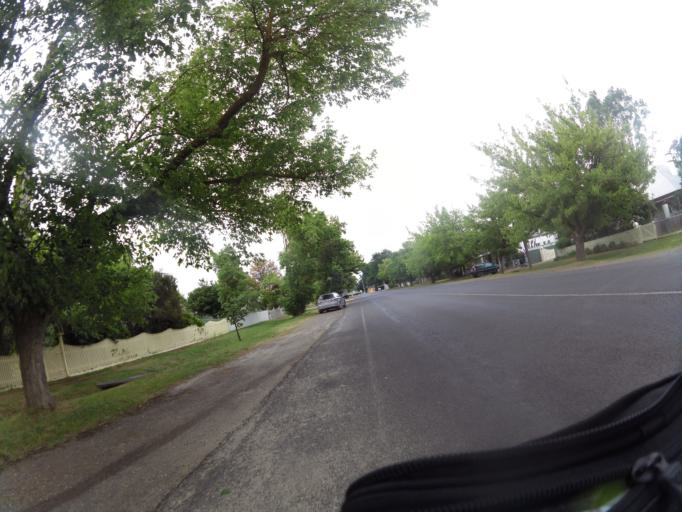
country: AU
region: Victoria
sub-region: Mount Alexander
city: Castlemaine
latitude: -37.0677
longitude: 144.2121
